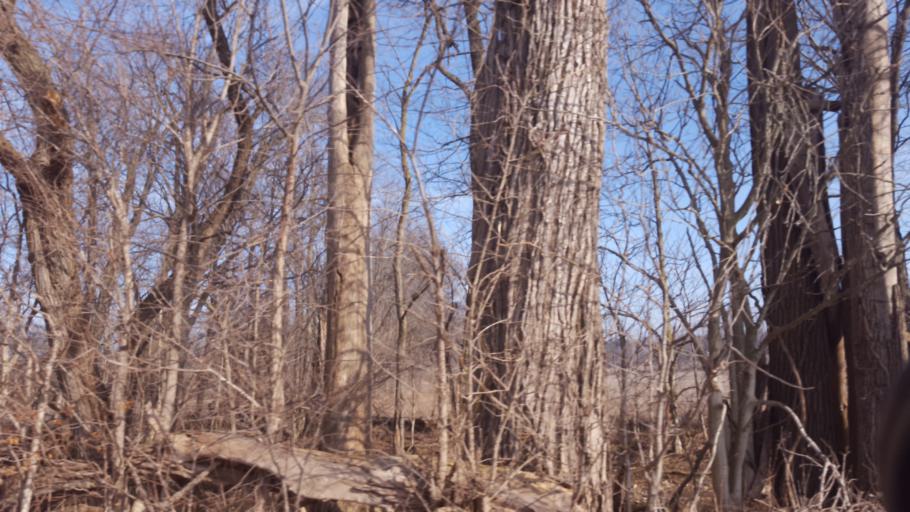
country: US
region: Ohio
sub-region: Crawford County
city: Crestline
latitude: 40.7034
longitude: -82.6892
